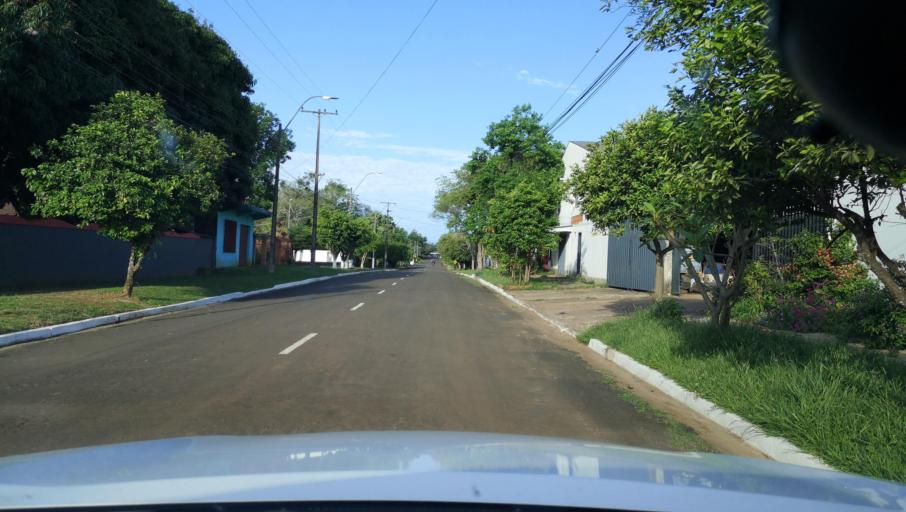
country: PY
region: Itapua
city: Carmen del Parana
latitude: -27.1600
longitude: -56.2366
